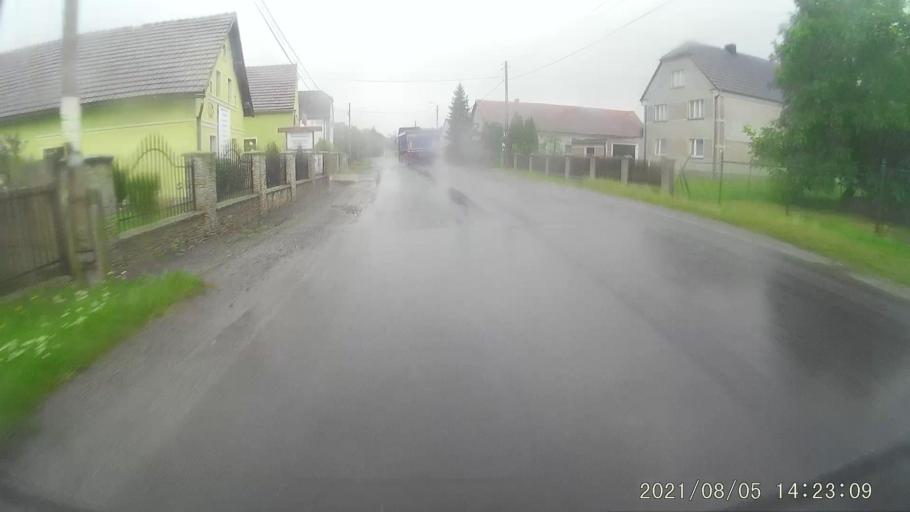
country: PL
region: Opole Voivodeship
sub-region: Powiat nyski
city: Korfantow
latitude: 50.4805
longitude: 17.6496
